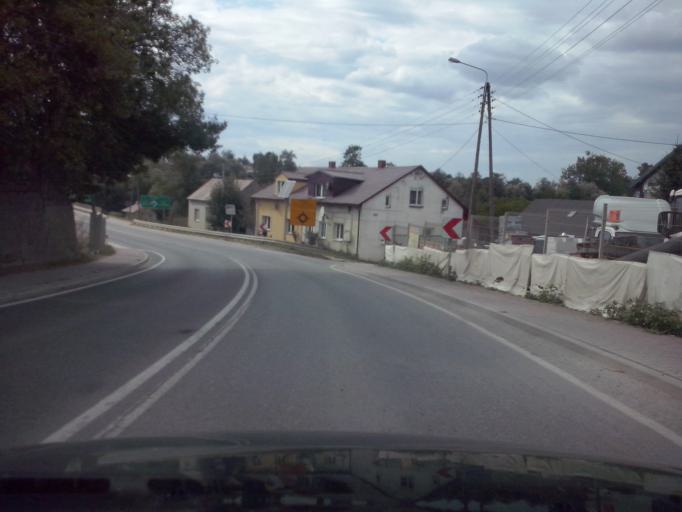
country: PL
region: Swietokrzyskie
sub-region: Powiat kielecki
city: Lagow
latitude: 50.7767
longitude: 21.0894
